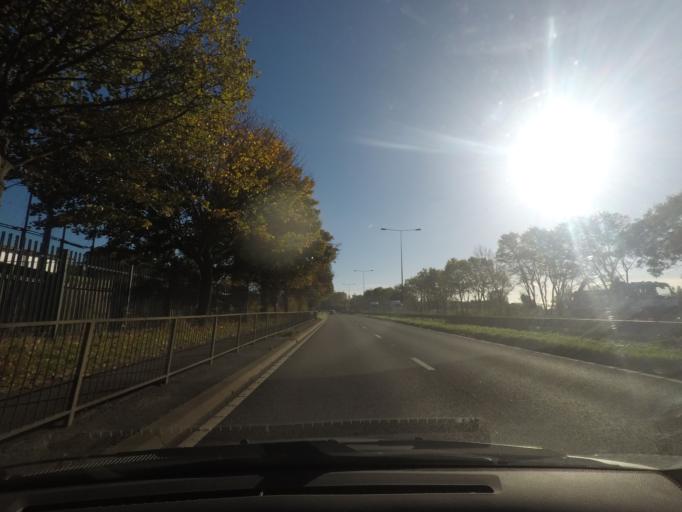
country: GB
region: England
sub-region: East Riding of Yorkshire
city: Welton
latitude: 53.7267
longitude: -0.5370
